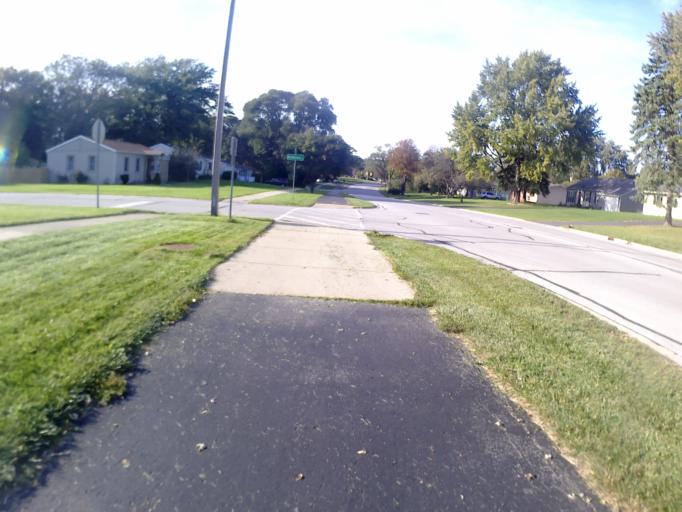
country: US
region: Illinois
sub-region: DuPage County
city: Woodridge
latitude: 41.7468
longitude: -88.0506
